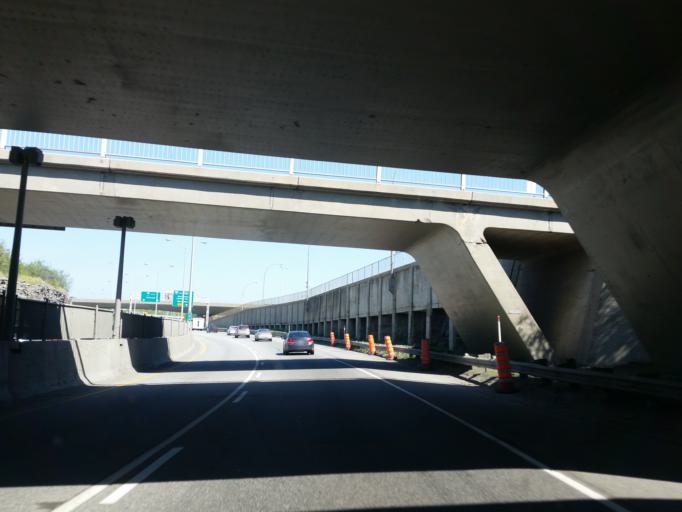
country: CA
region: Ontario
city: Ottawa
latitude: 45.4409
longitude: -75.7281
